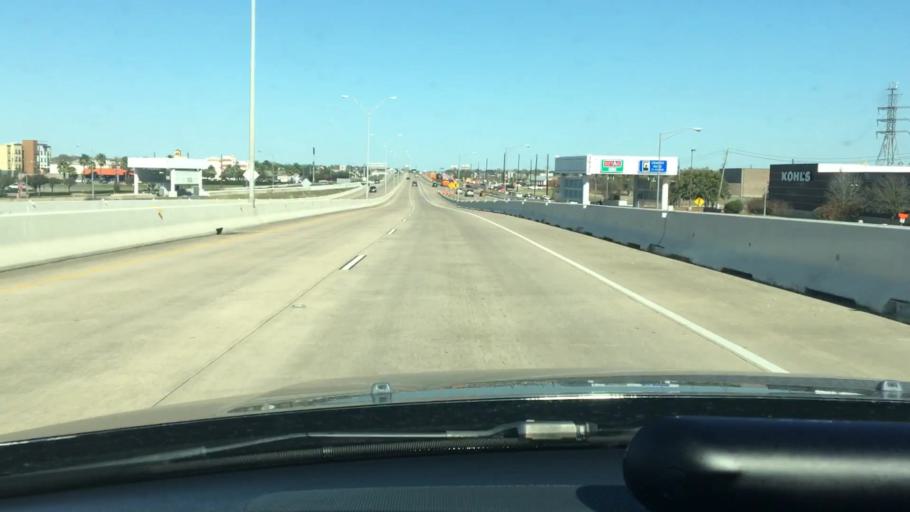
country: US
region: Texas
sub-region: Harris County
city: Deer Park
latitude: 29.6515
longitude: -95.1560
